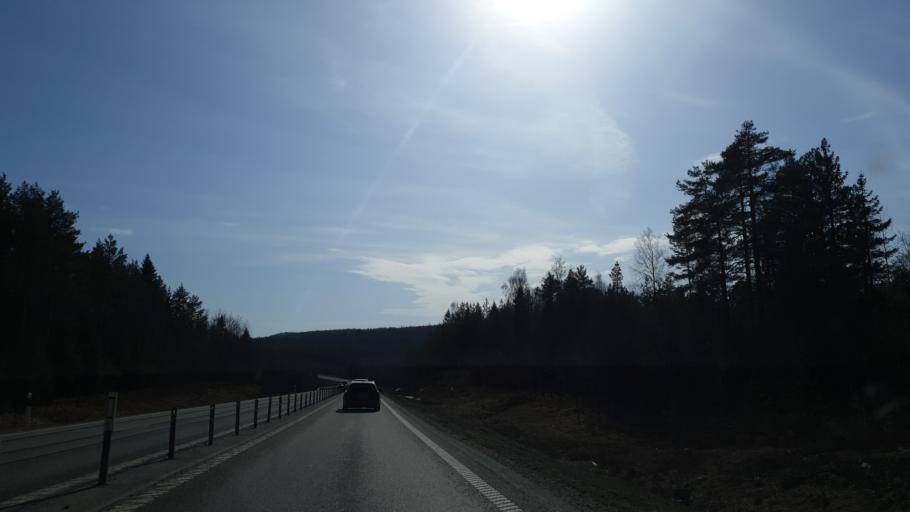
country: SE
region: Vaesternorrland
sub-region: Sundsvalls Kommun
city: Njurundabommen
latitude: 62.1918
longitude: 17.3649
